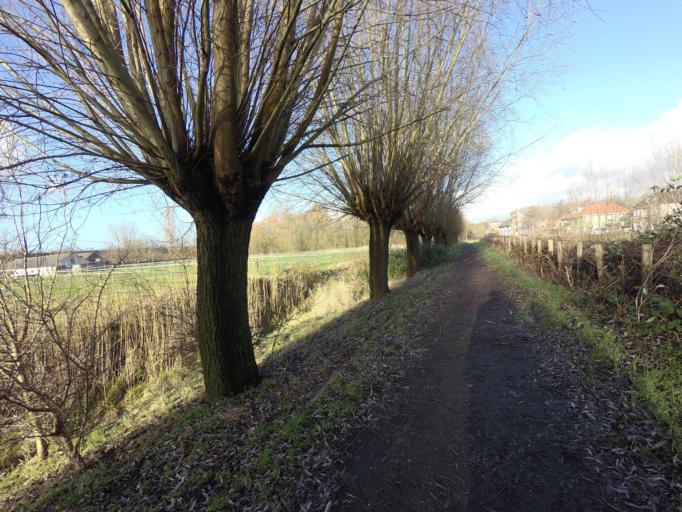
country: NL
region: Utrecht
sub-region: Gemeente Nieuwegein
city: Nieuwegein
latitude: 52.0555
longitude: 5.0705
